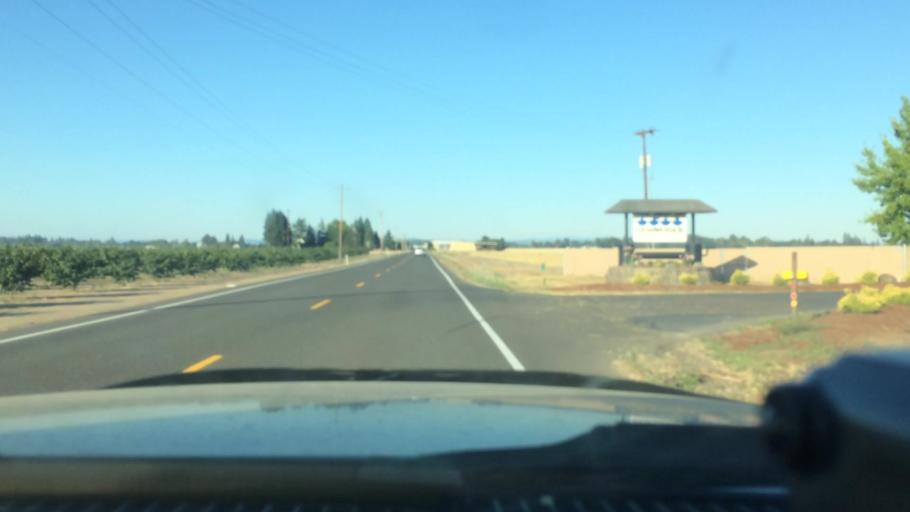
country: US
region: Oregon
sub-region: Yamhill County
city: Newberg
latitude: 45.2364
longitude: -122.9599
